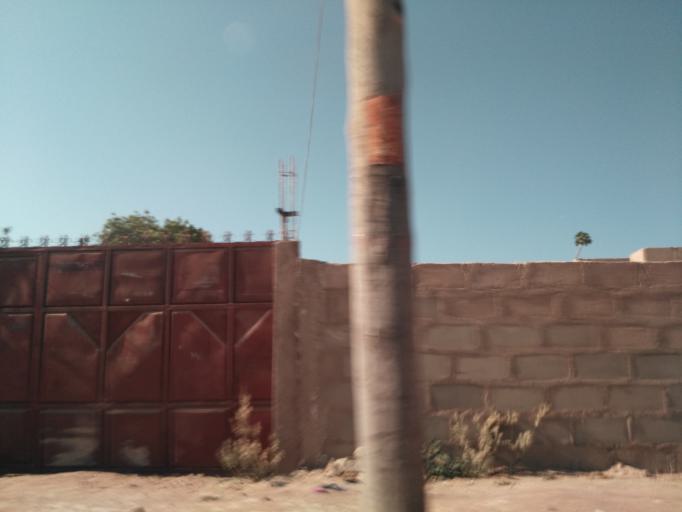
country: TZ
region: Dodoma
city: Dodoma
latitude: -6.1299
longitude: 35.7423
